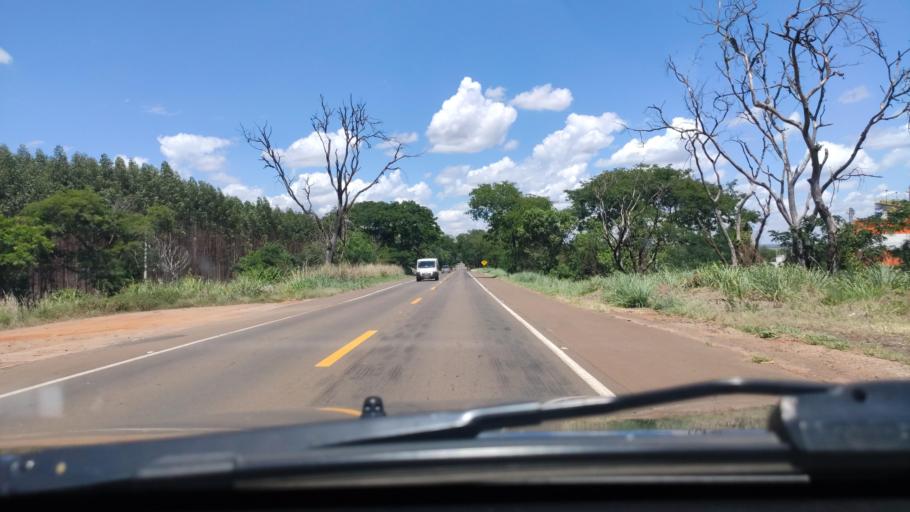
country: BR
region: Sao Paulo
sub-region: Boa Esperanca Do Sul
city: Boa Esperanca do Sul
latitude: -22.0690
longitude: -48.3740
